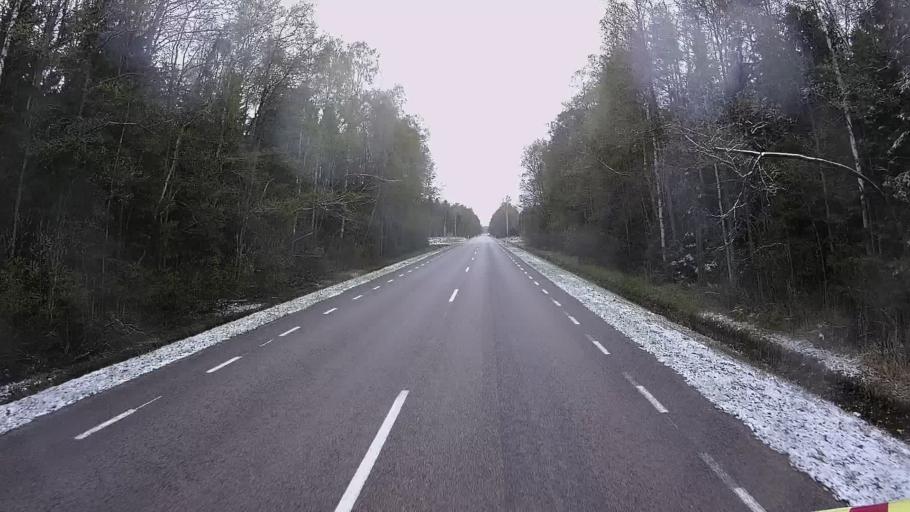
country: EE
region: Hiiumaa
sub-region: Kaerdla linn
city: Kardla
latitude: 58.8430
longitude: 22.4677
